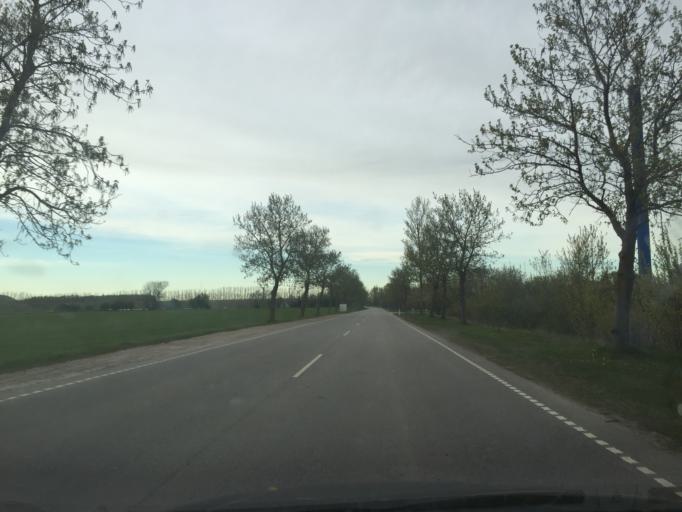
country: DK
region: Capital Region
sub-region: Hoje-Taastrup Kommune
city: Taastrup
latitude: 55.6587
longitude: 12.2536
